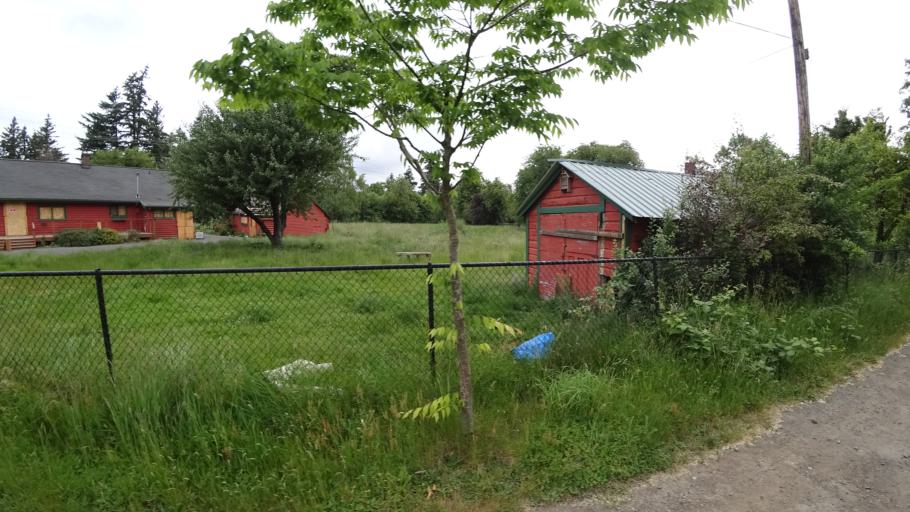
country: US
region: Oregon
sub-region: Multnomah County
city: Lents
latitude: 45.4668
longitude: -122.5739
